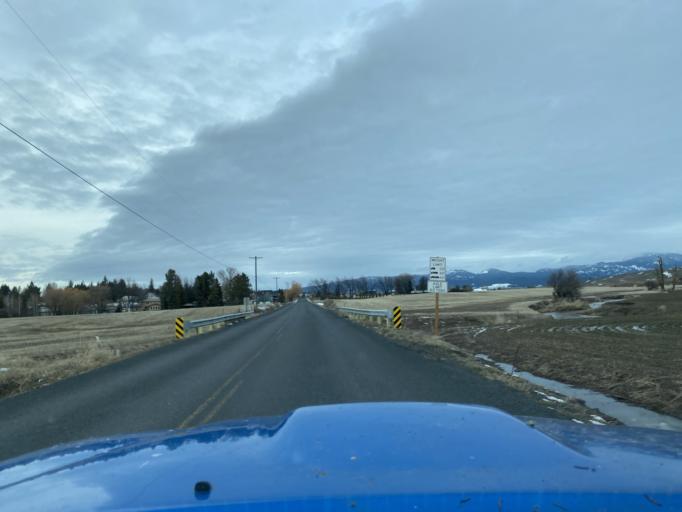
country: US
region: Idaho
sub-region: Latah County
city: Moscow
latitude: 46.7131
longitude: -116.9591
